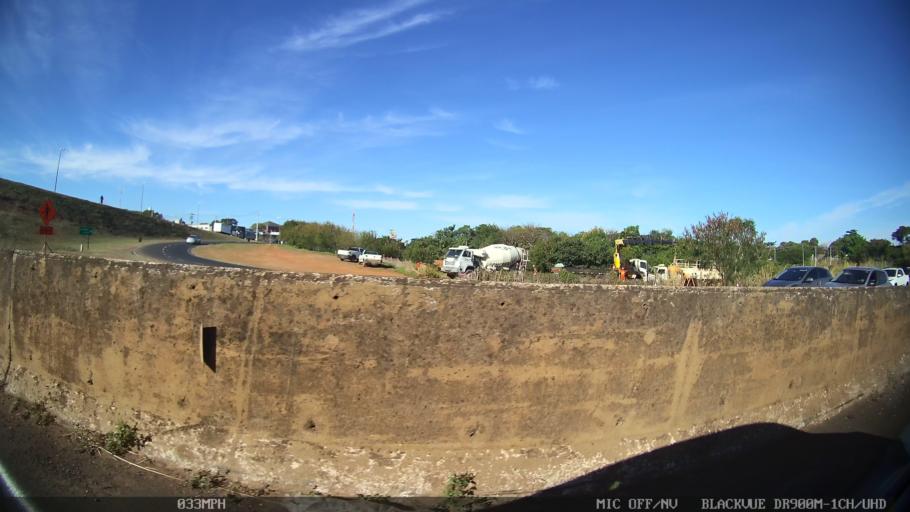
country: BR
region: Sao Paulo
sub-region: Sao Jose Do Rio Preto
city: Sao Jose do Rio Preto
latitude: -20.8098
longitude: -49.3564
